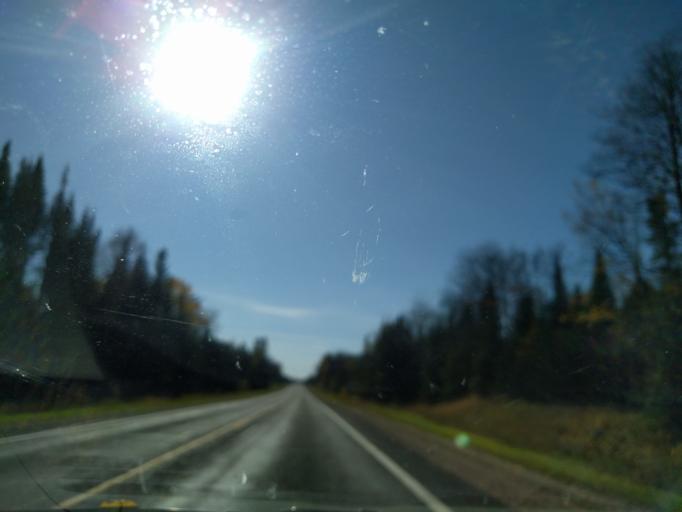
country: US
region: Michigan
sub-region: Iron County
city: Crystal Falls
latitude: 46.1650
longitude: -88.0748
